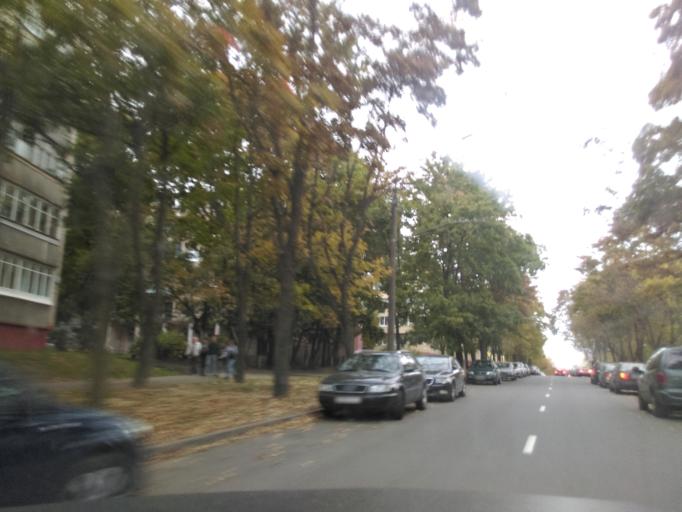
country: BY
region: Minsk
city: Minsk
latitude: 53.9119
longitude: 27.5941
